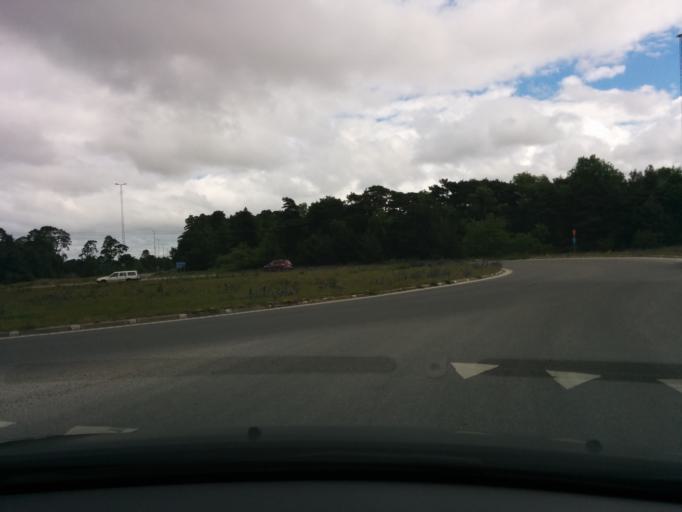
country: SE
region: Gotland
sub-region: Gotland
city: Visby
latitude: 57.6248
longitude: 18.3213
